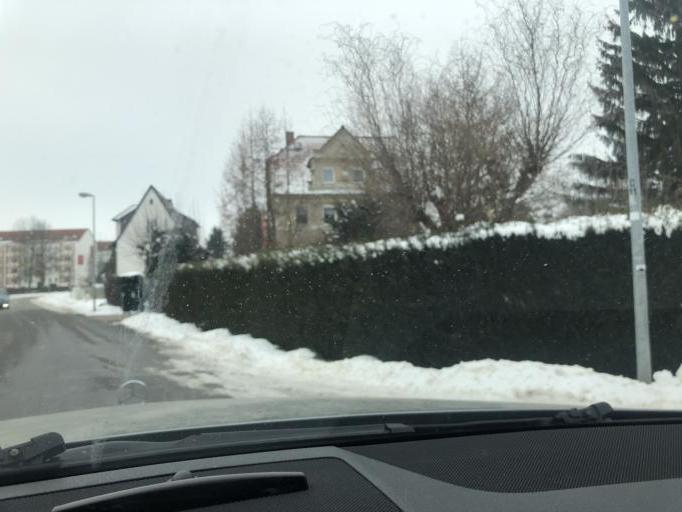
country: DE
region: Brandenburg
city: Guben
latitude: 51.9438
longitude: 14.7120
